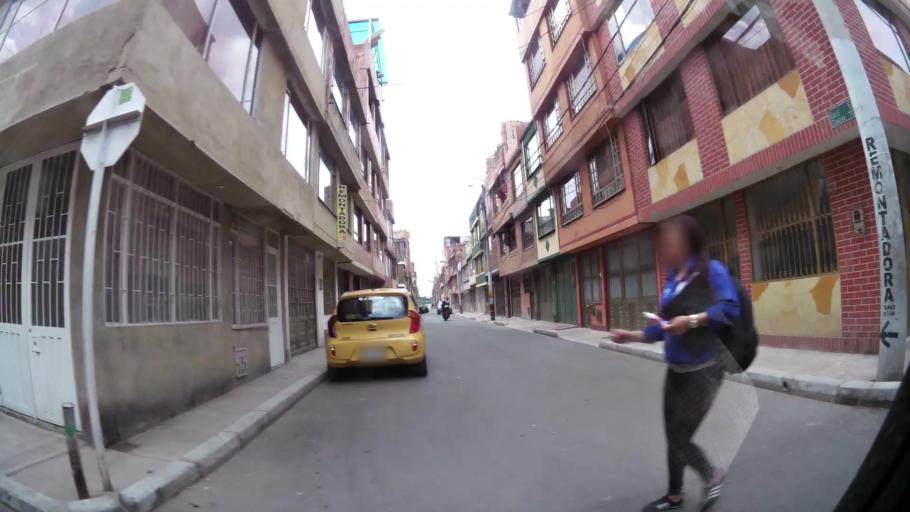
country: CO
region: Cundinamarca
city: Funza
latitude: 4.7115
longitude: -74.1433
